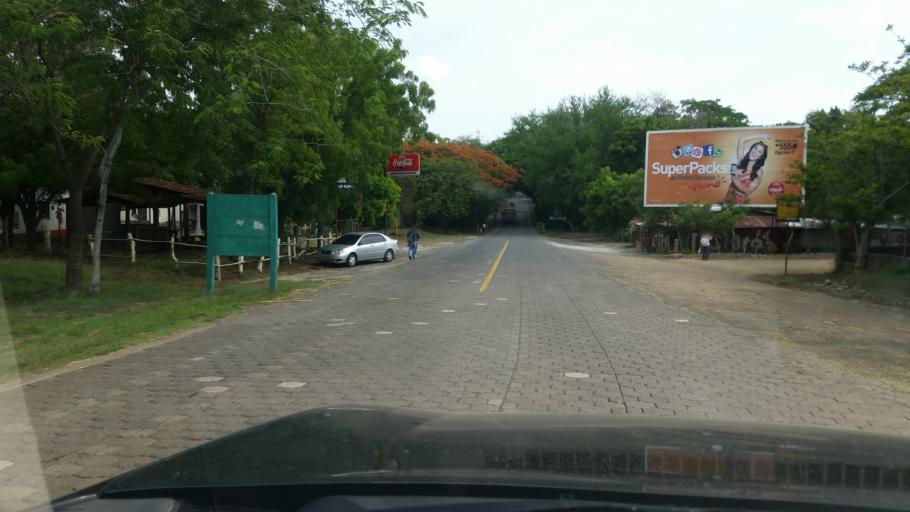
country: NI
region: Managua
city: Carlos Fonseca Amador
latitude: 12.0720
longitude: -86.4994
